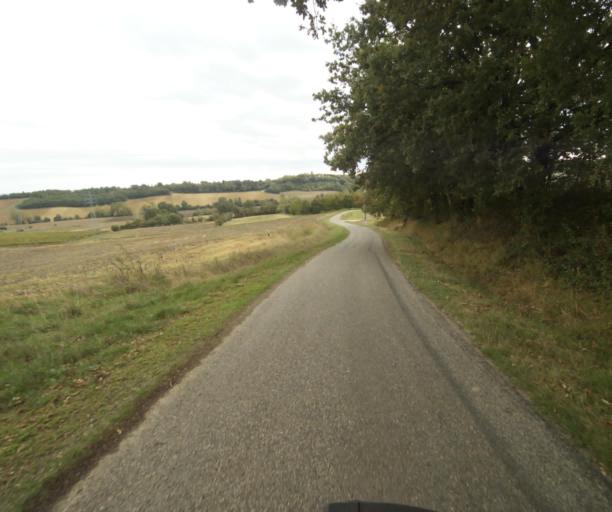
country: FR
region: Midi-Pyrenees
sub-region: Departement du Tarn-et-Garonne
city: Verdun-sur-Garonne
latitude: 43.8526
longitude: 1.1119
